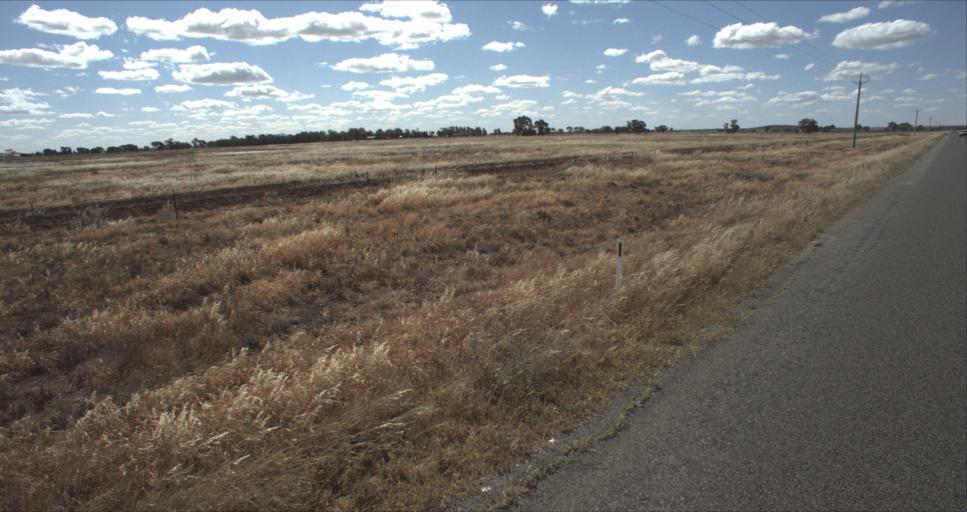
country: AU
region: New South Wales
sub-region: Leeton
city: Leeton
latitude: -34.4705
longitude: 146.2510
